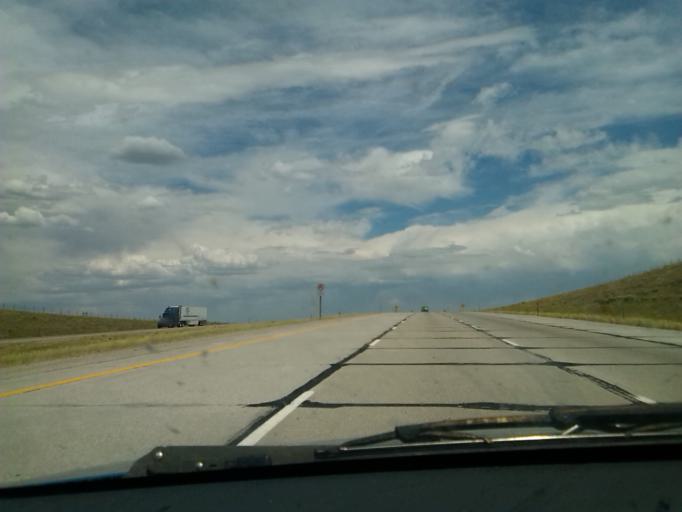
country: US
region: Wyoming
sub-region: Carbon County
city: Saratoga
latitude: 41.7333
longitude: -106.6474
